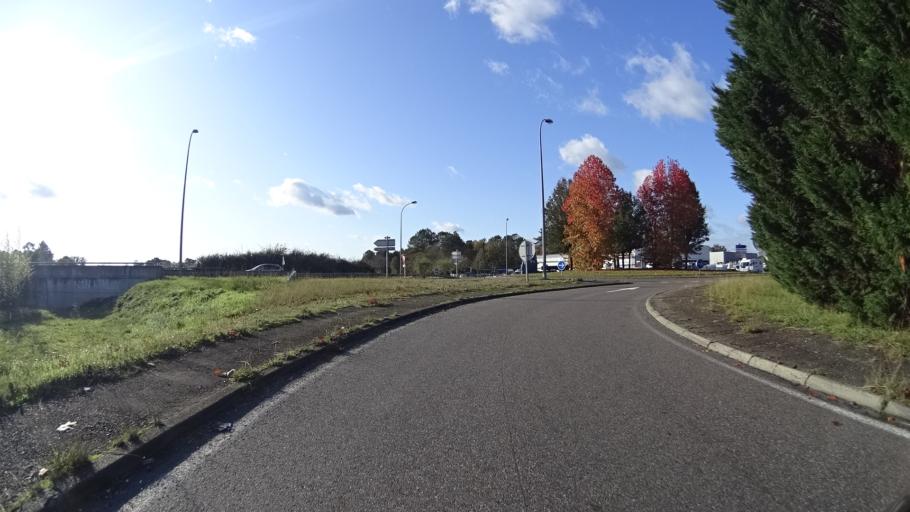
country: FR
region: Aquitaine
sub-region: Departement des Landes
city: Saint-Paul-les-Dax
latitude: 43.7451
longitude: -1.0549
